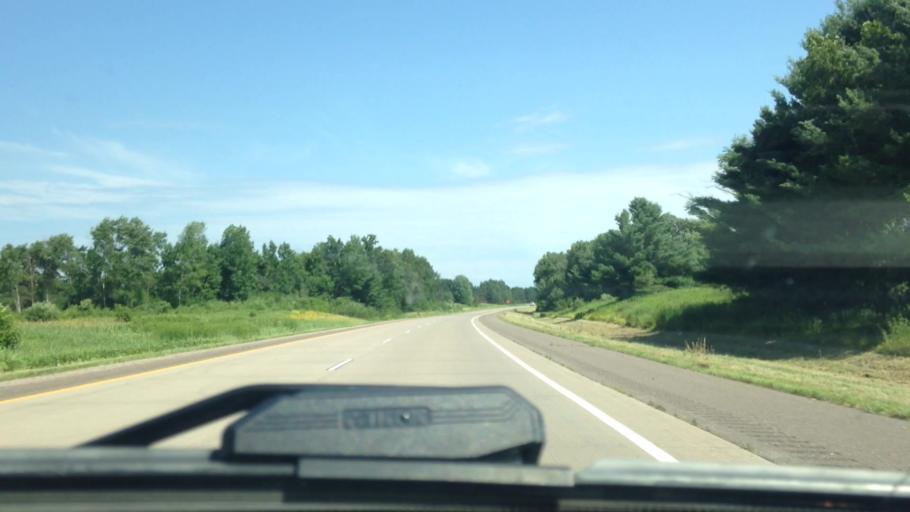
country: US
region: Wisconsin
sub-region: Barron County
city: Rice Lake
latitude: 45.5564
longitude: -91.7653
